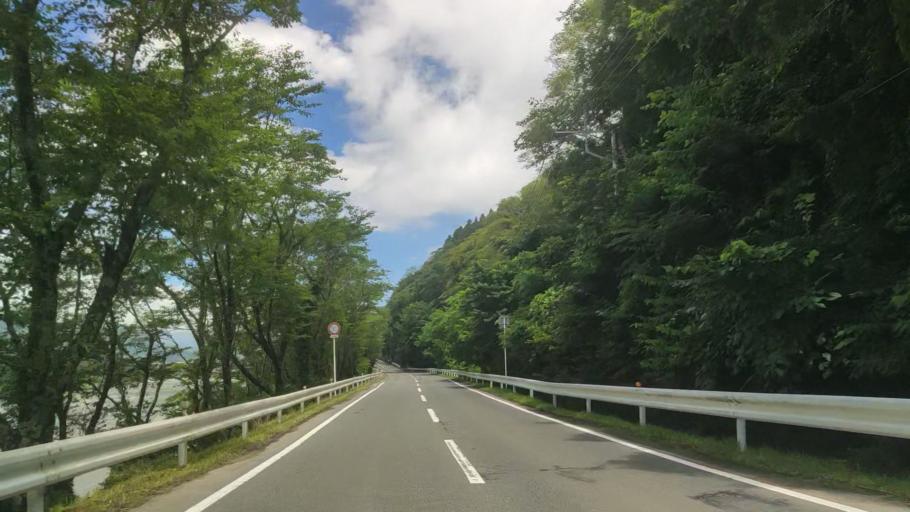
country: JP
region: Shizuoka
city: Fujinomiya
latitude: 35.2971
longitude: 138.4564
